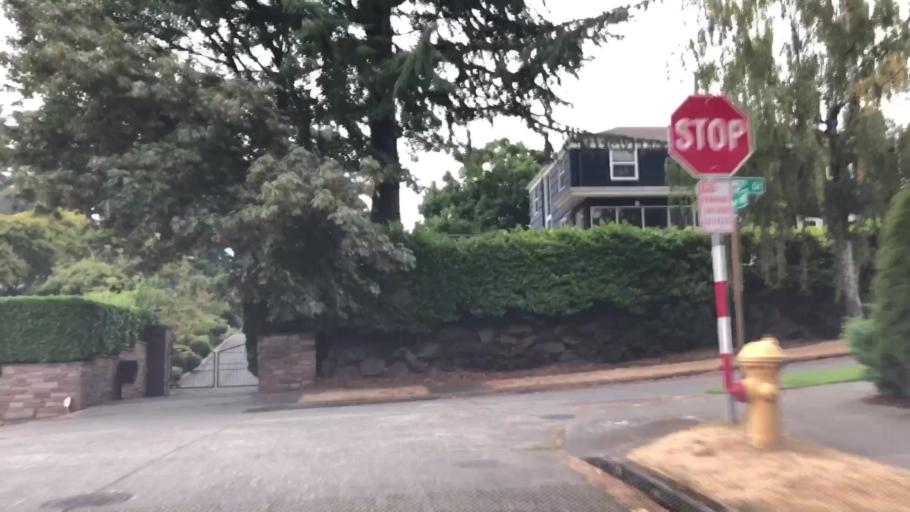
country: US
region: Washington
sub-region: King County
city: Yarrow Point
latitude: 47.6610
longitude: -122.2730
